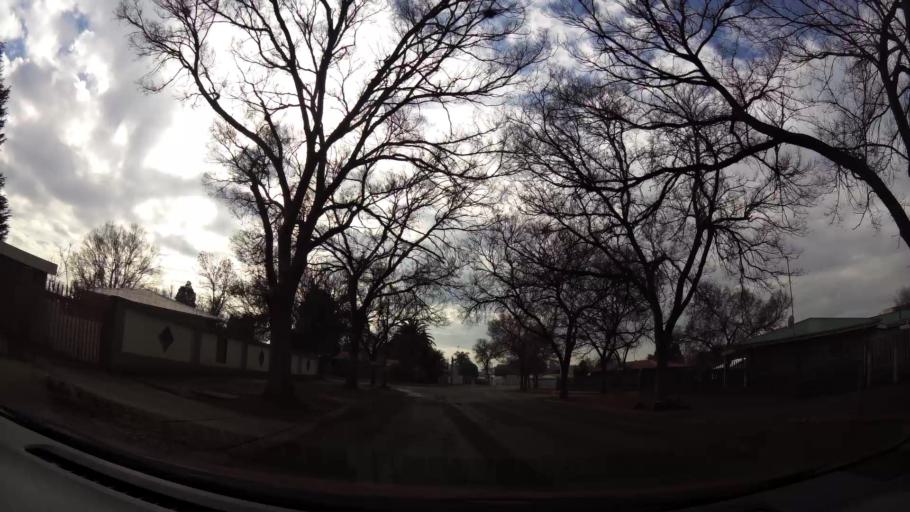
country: ZA
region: Gauteng
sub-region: Sedibeng District Municipality
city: Vanderbijlpark
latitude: -26.7019
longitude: 27.8301
